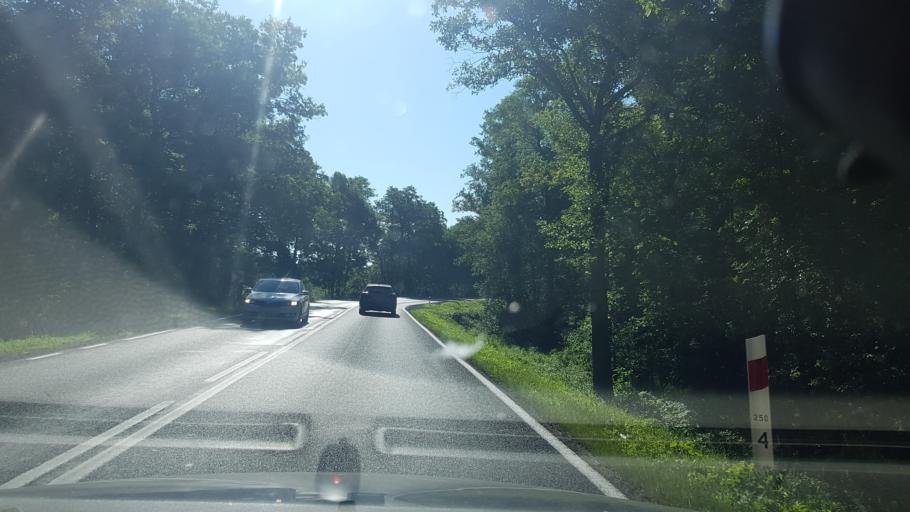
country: PL
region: Masovian Voivodeship
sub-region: Powiat wyszkowski
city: Wyszkow
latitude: 52.5861
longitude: 21.5201
